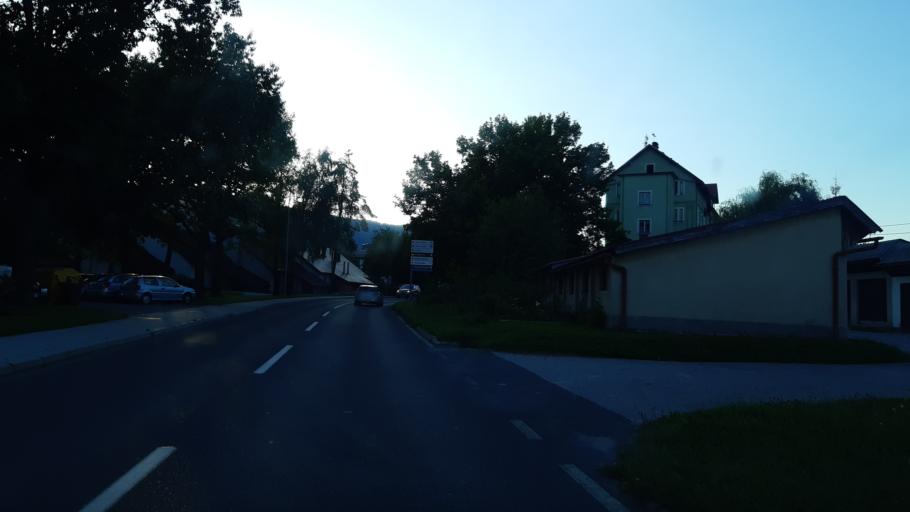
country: SI
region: Kocevje
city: Kocevje
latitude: 45.6436
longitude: 14.8592
